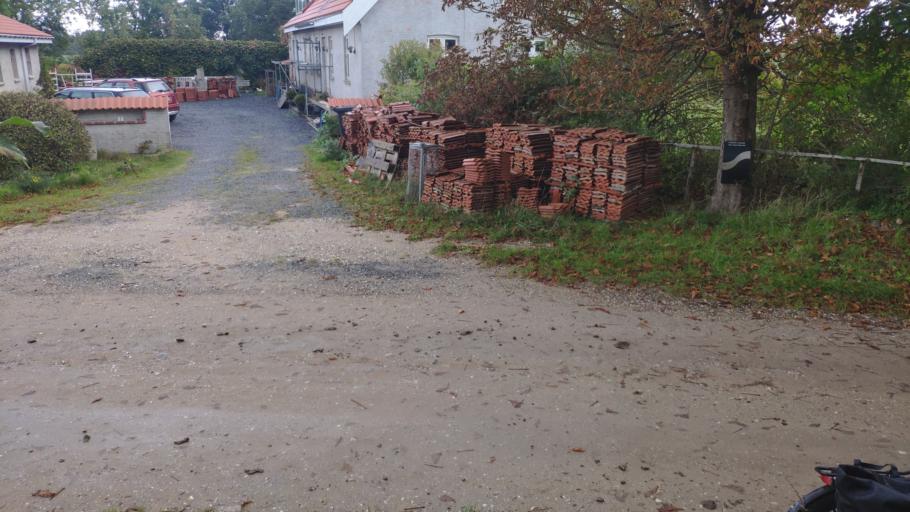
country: DK
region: Capital Region
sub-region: Frederikssund Kommune
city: Skibby
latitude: 55.7865
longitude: 11.8870
